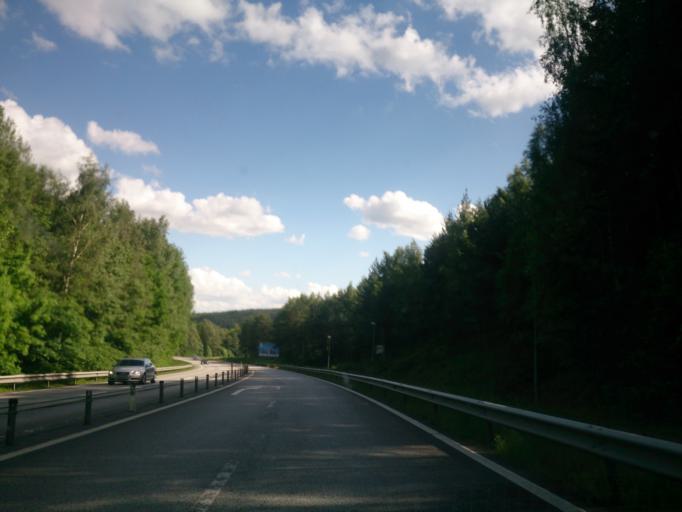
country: SE
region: OEstergoetland
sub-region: Norrkopings Kommun
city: Jursla
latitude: 58.6782
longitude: 16.1493
